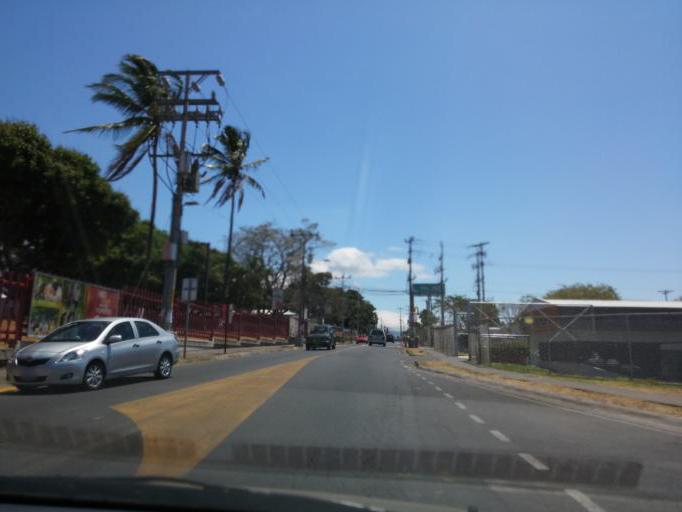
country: CR
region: Alajuela
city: Alajuela
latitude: 10.0133
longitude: -84.2237
